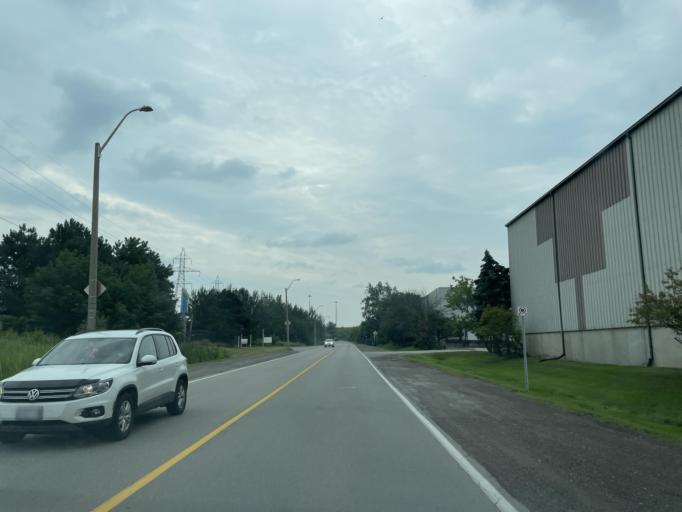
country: CA
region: Ontario
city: Hamilton
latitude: 43.2515
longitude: -79.7607
